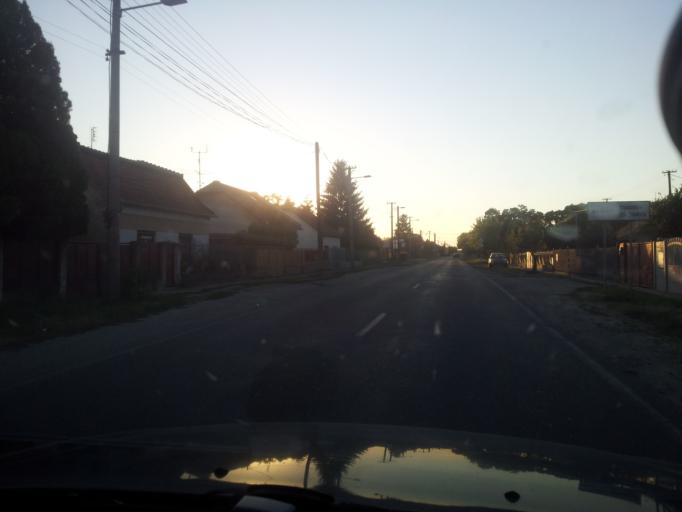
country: SK
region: Nitriansky
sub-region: Okres Nove Zamky
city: Sturovo
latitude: 47.8109
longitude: 18.7029
